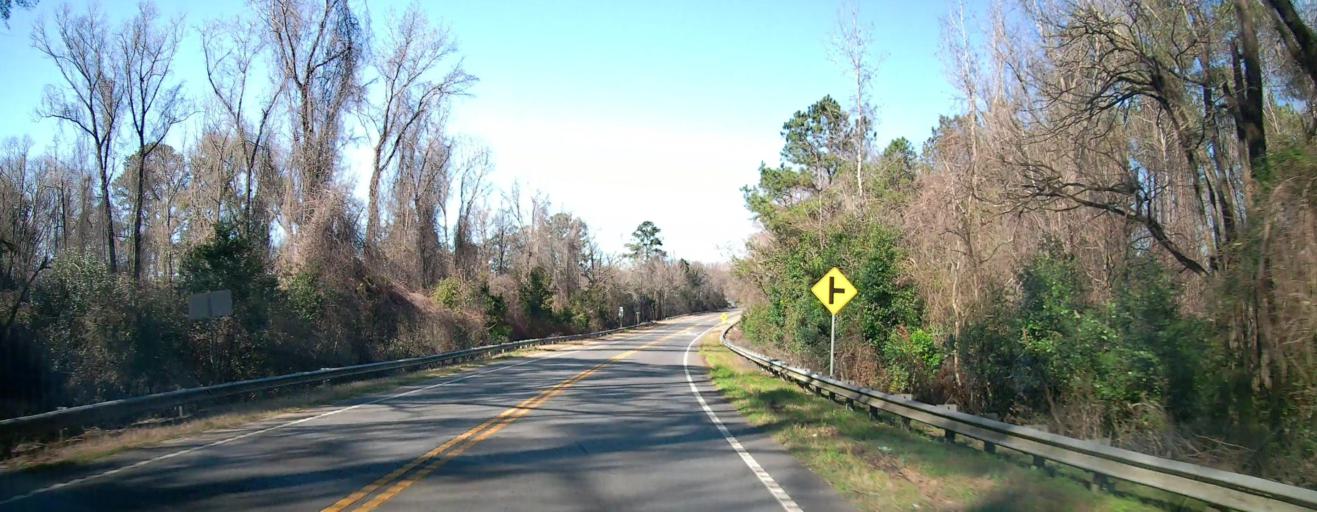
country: US
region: Georgia
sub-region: Macon County
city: Oglethorpe
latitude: 32.3074
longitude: -84.0657
